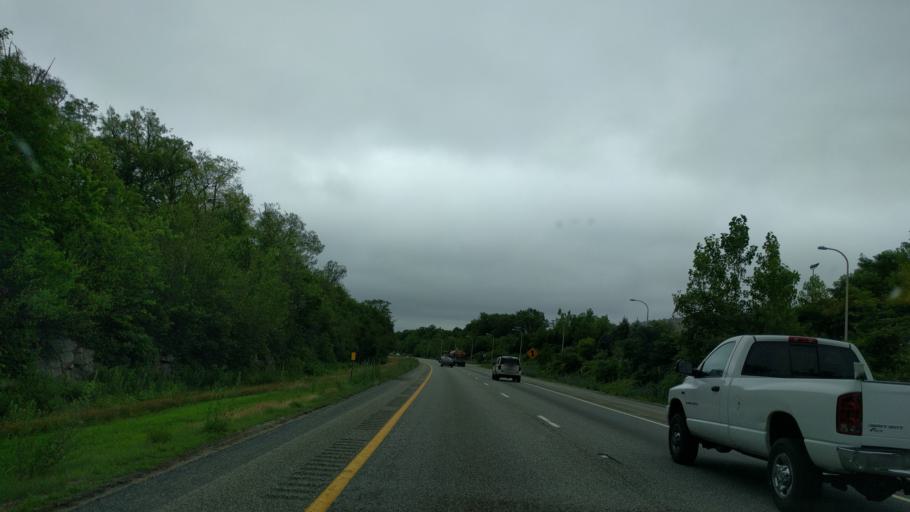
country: US
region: Rhode Island
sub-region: Providence County
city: Johnston
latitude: 41.8039
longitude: -71.5110
